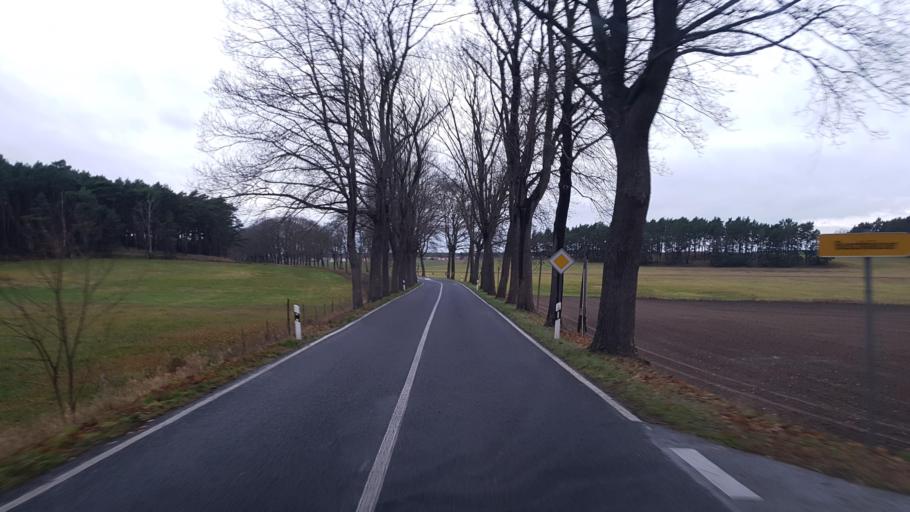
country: DE
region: Brandenburg
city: Tauche
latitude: 52.0750
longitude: 14.0718
